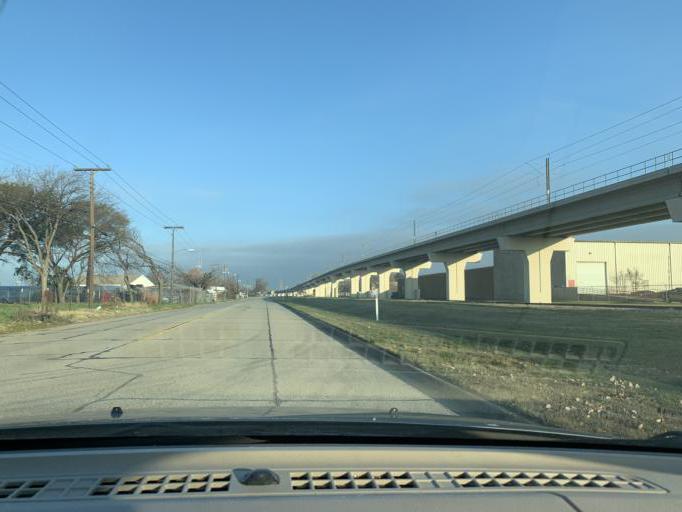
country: US
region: Texas
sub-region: Dallas County
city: Carrollton
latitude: 32.9654
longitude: -96.9159
